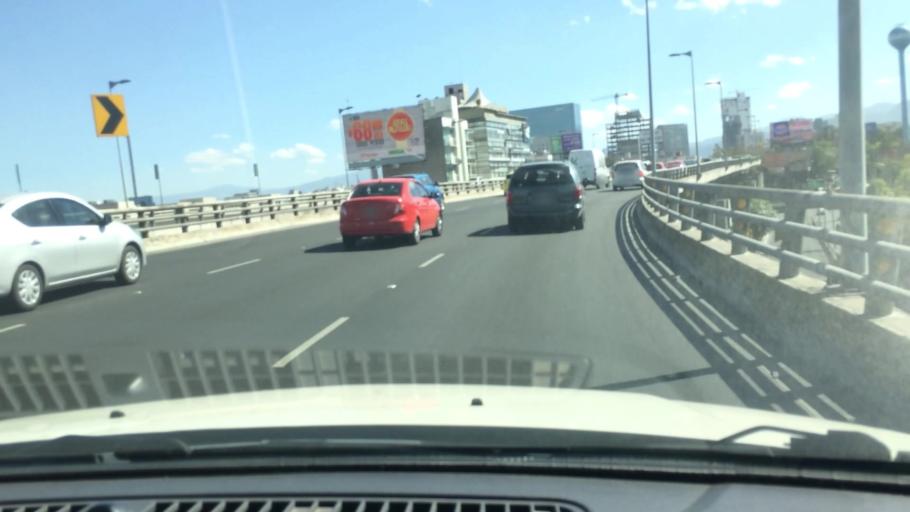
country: MX
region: Mexico City
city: Alvaro Obregon
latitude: 19.3707
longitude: -99.1937
